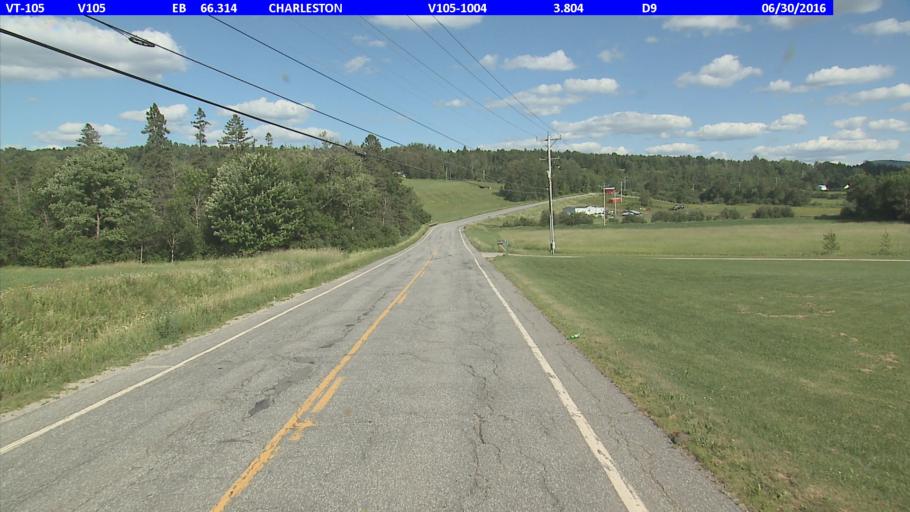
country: US
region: Vermont
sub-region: Orleans County
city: Newport
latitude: 44.8640
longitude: -72.0412
